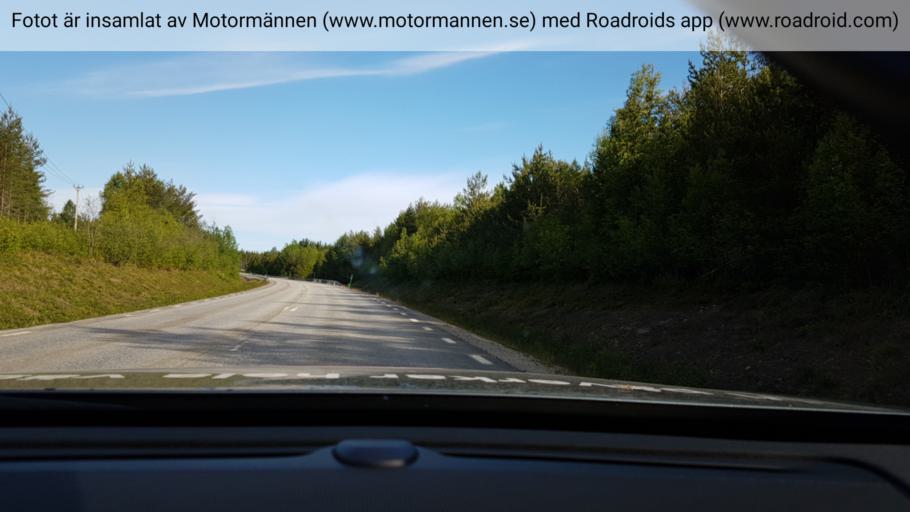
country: SE
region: Vaesterbotten
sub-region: Vannas Kommun
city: Vaennaes
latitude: 63.9441
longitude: 19.7680
